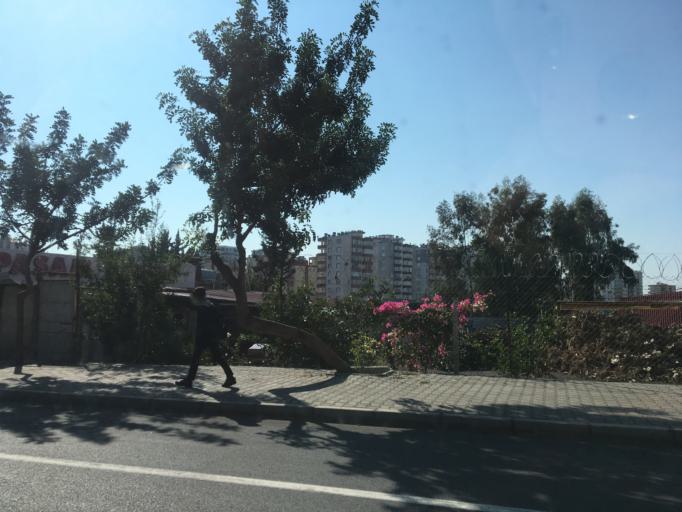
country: TR
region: Adana
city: Seyhan
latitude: 37.0363
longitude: 35.2805
